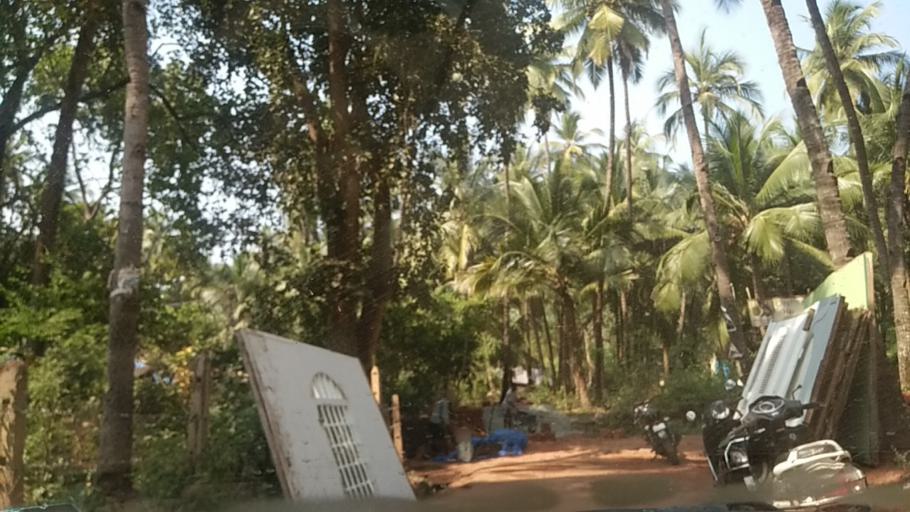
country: IN
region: Goa
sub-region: South Goa
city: Kankon
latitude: 15.0146
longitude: 74.0188
